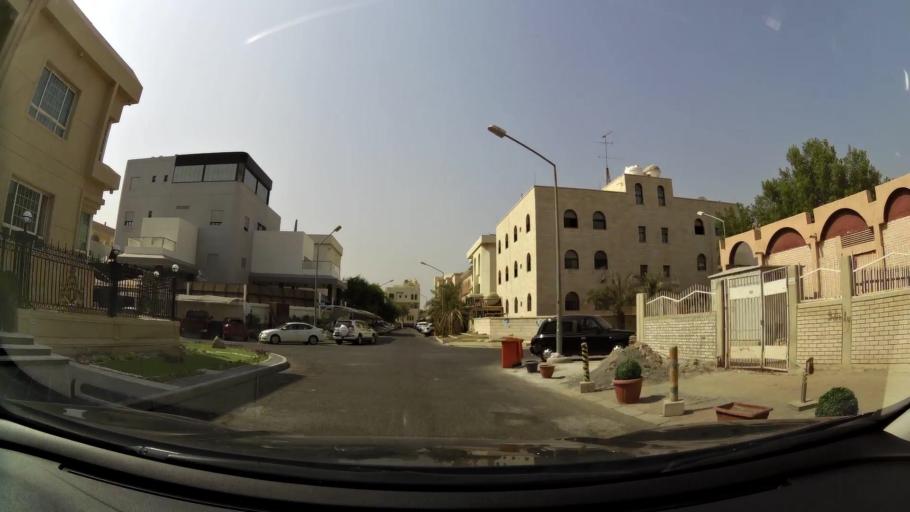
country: KW
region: Al Asimah
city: Ad Dasmah
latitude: 29.3550
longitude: 48.0091
